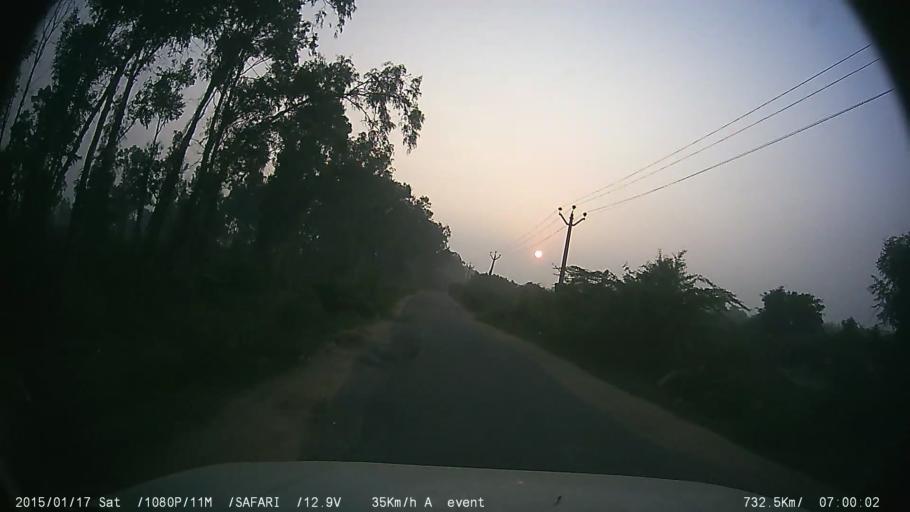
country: IN
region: Tamil Nadu
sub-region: Kancheepuram
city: Singapperumalkovil
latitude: 12.7974
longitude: 80.0115
